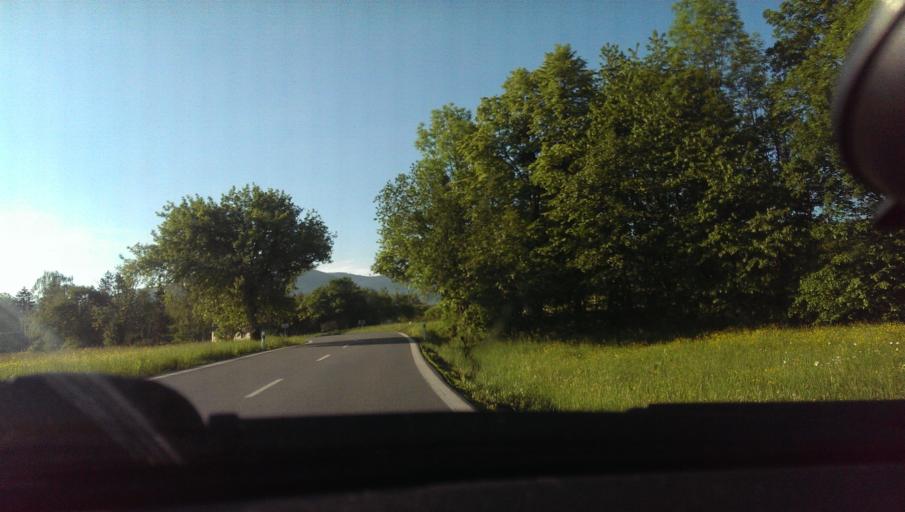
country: CZ
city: Kuncice pod Ondrejnikem
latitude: 49.5453
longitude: 18.2605
